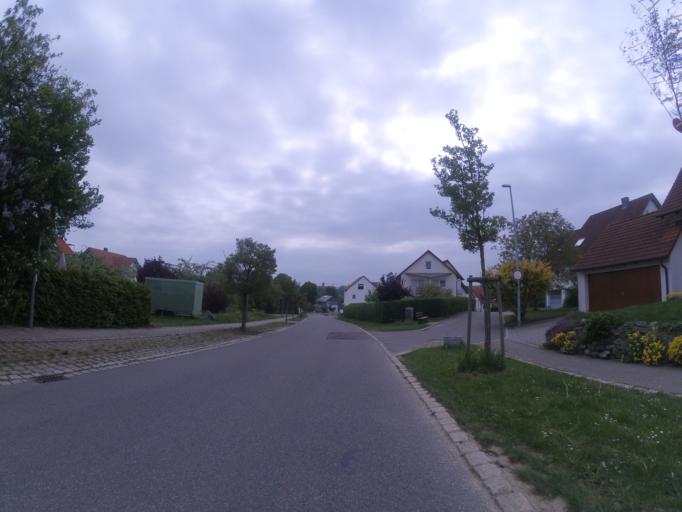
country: DE
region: Baden-Wuerttemberg
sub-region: Tuebingen Region
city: Staig
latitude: 48.3009
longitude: 9.9872
